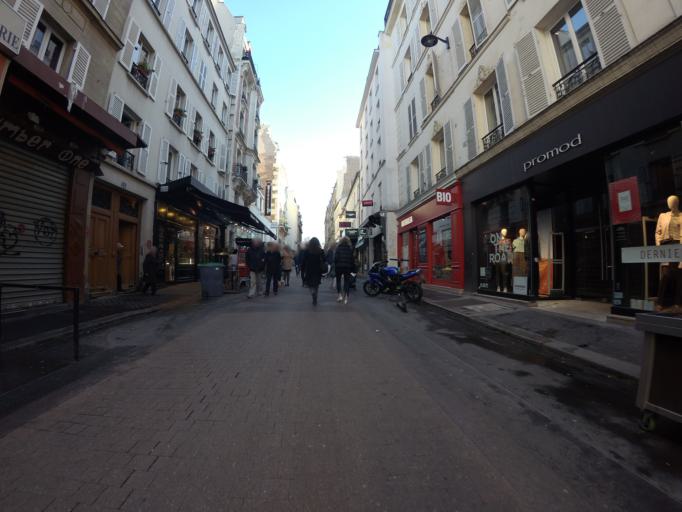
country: FR
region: Ile-de-France
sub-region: Departement des Hauts-de-Seine
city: Clichy
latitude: 48.8825
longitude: 2.3151
